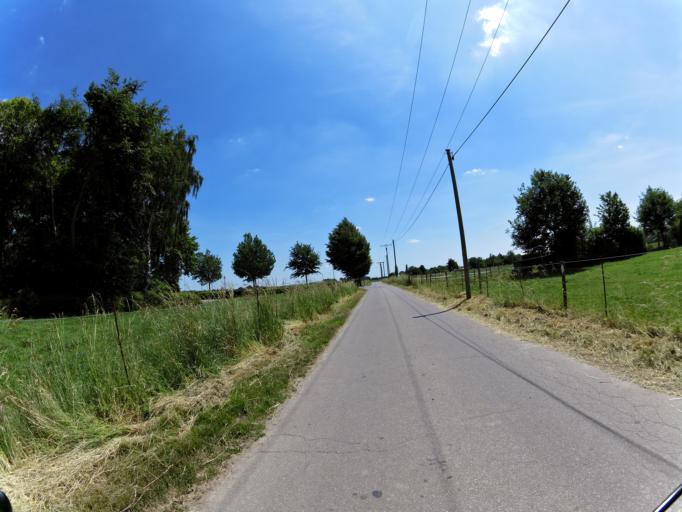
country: DE
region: North Rhine-Westphalia
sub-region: Regierungsbezirk Koln
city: Heinsberg
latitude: 51.0177
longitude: 6.0762
